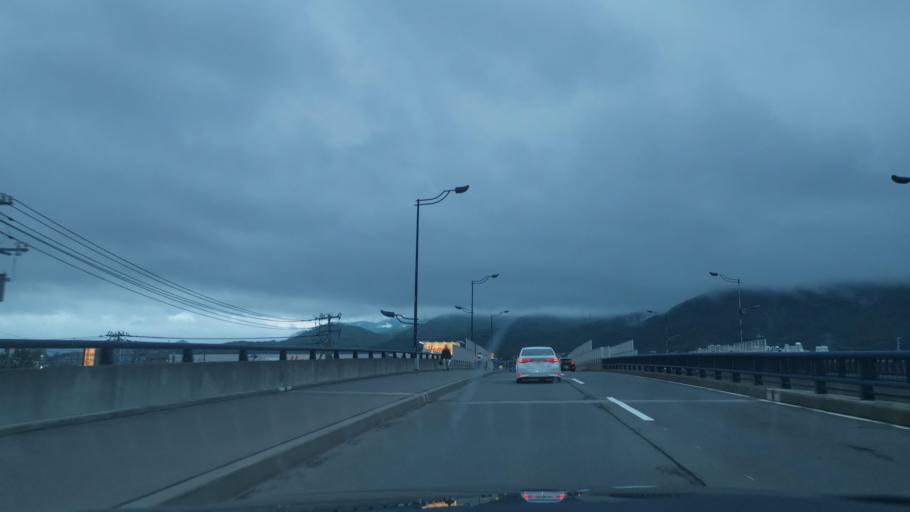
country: JP
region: Hokkaido
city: Sapporo
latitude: 43.1040
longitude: 141.2723
